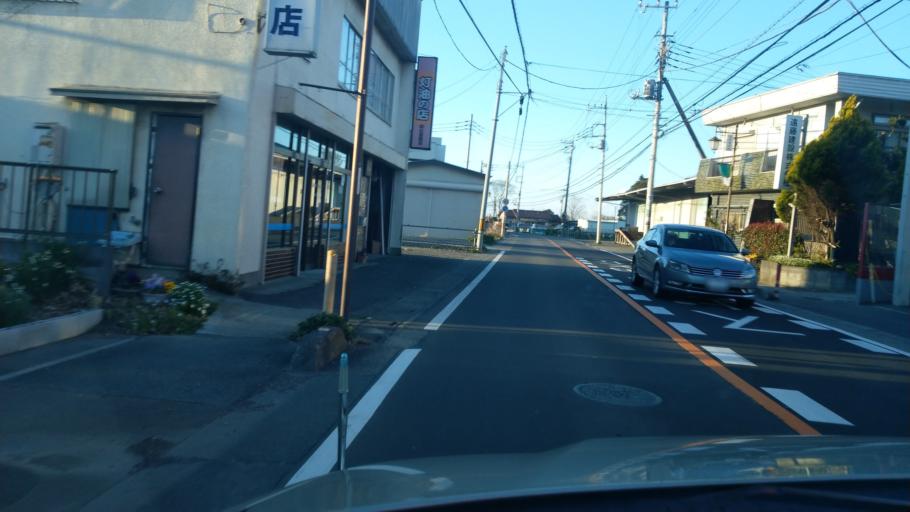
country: JP
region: Saitama
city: Okegawa
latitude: 35.9306
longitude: 139.5575
